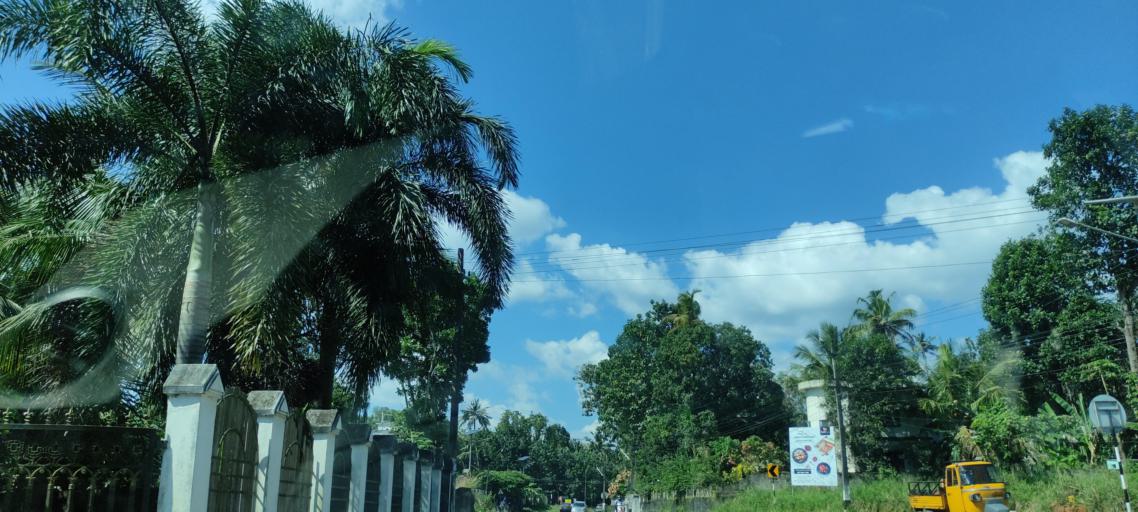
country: IN
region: Kerala
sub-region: Pattanamtitta
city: Adur
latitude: 9.1415
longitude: 76.7343
